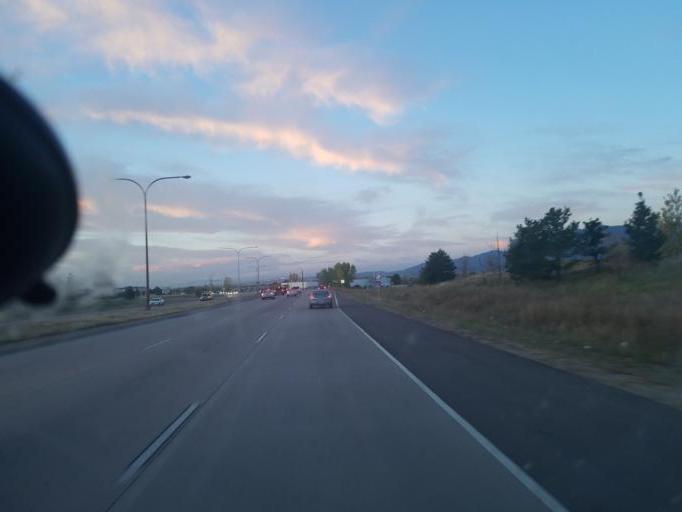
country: US
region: Colorado
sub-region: El Paso County
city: Cimarron Hills
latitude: 38.8187
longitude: -104.7287
